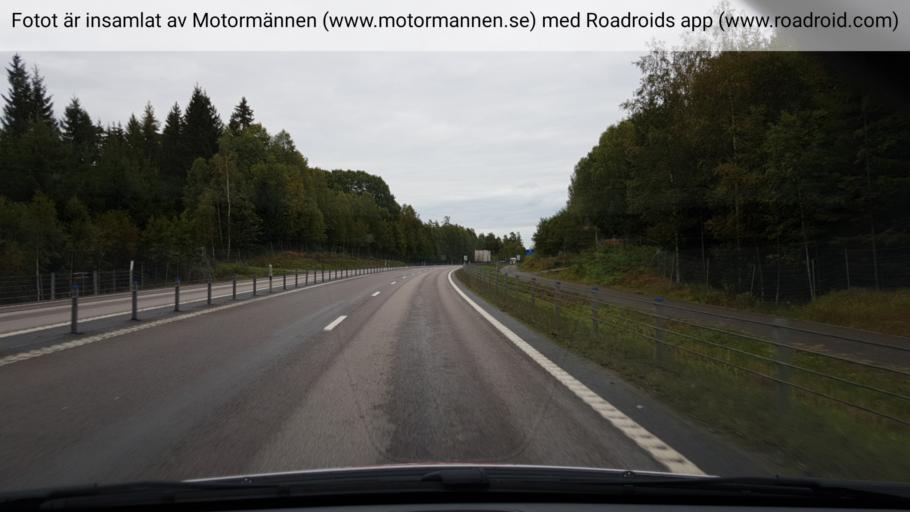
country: SE
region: Vaermland
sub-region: Karlstads Kommun
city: Valberg
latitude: 59.3706
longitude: 13.1593
